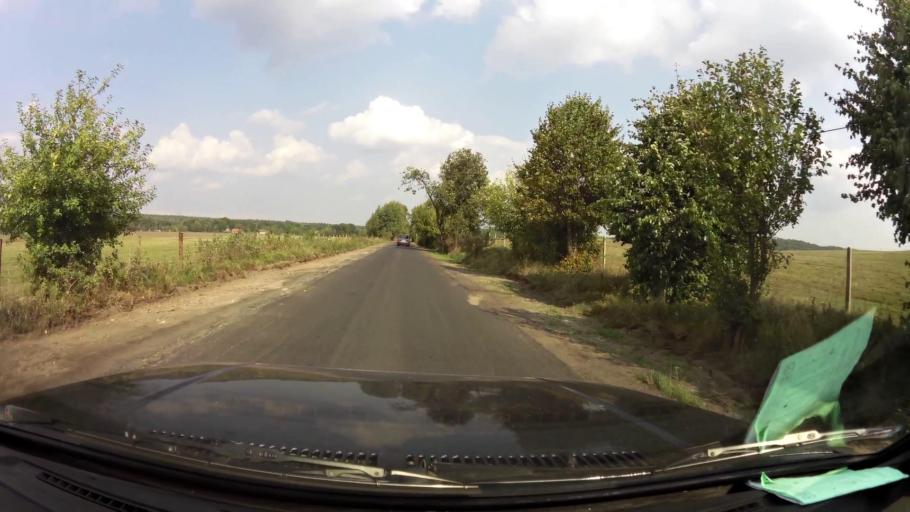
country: PL
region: West Pomeranian Voivodeship
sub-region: Powiat koszalinski
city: Bobolice
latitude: 54.1077
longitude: 16.4998
